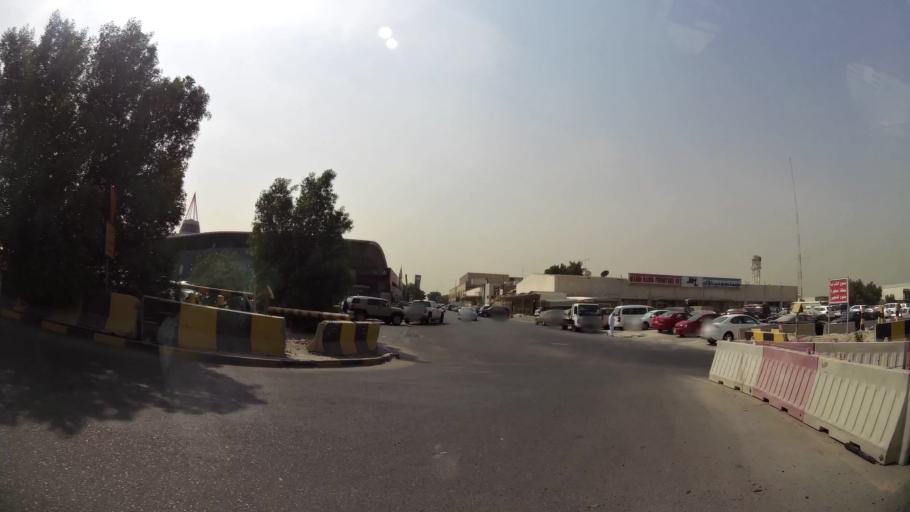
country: KW
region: Al Asimah
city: Ash Shamiyah
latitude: 29.3369
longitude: 47.9486
